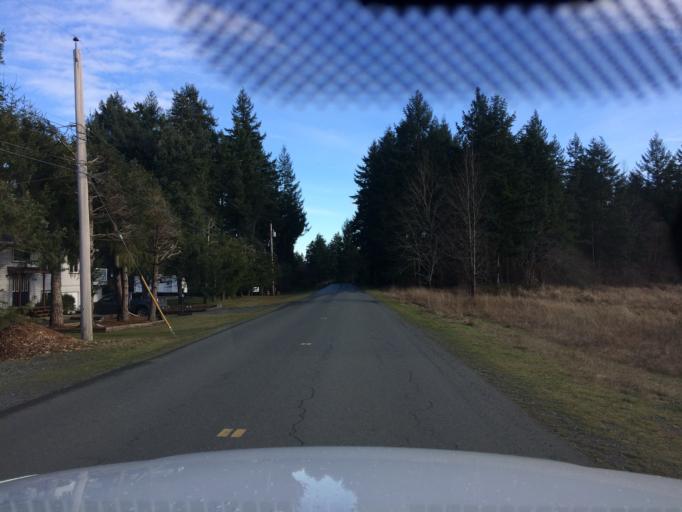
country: CA
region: British Columbia
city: Campbell River
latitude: 49.8881
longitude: -125.1309
